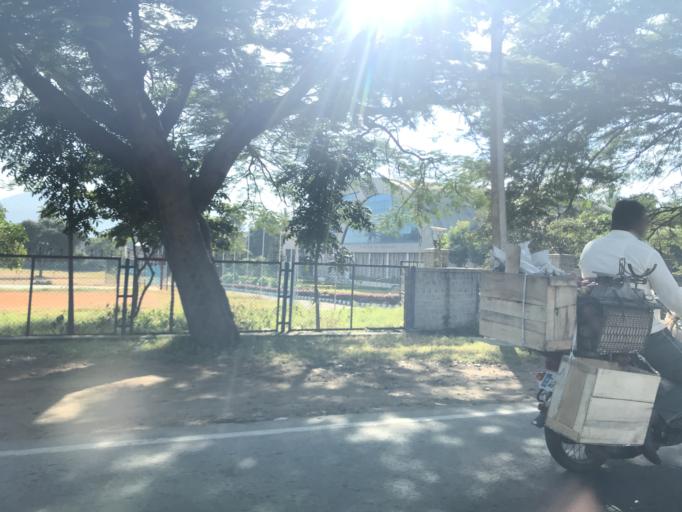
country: IN
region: Karnataka
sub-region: Mysore
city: Mysore
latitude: 12.2803
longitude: 76.6402
